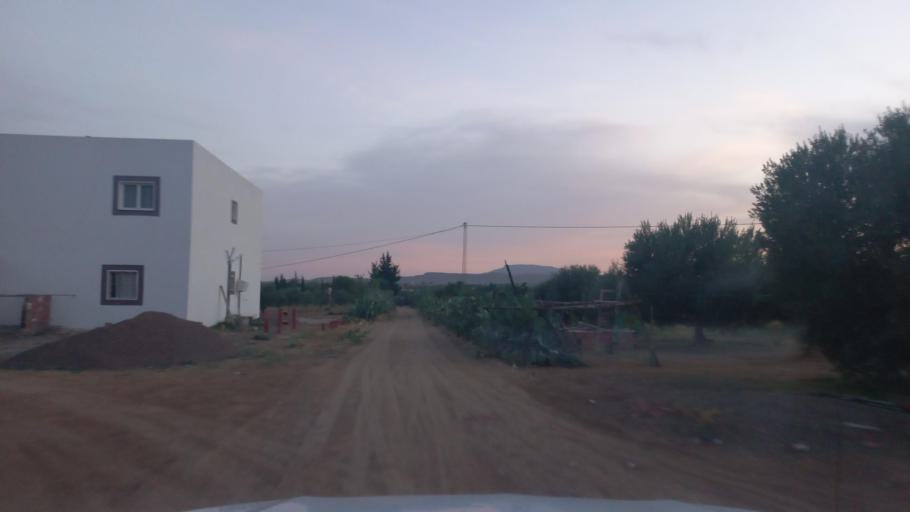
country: TN
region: Al Qasrayn
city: Kasserine
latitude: 35.2343
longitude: 9.0437
